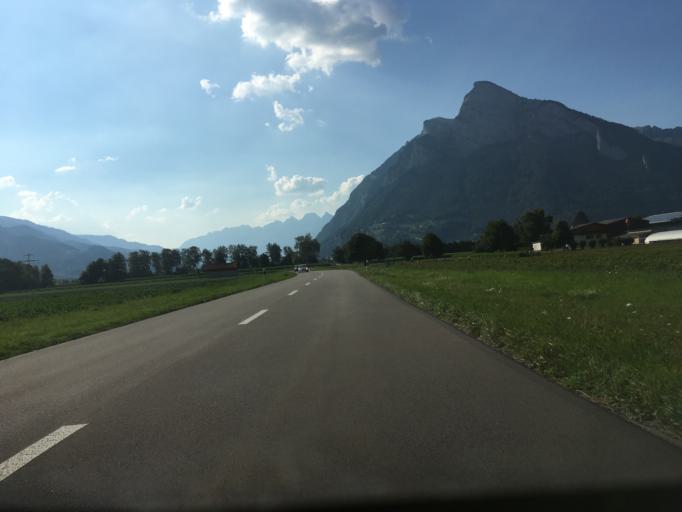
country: CH
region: Saint Gallen
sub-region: Wahlkreis Sarganserland
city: Sargans
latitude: 47.0301
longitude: 9.4647
